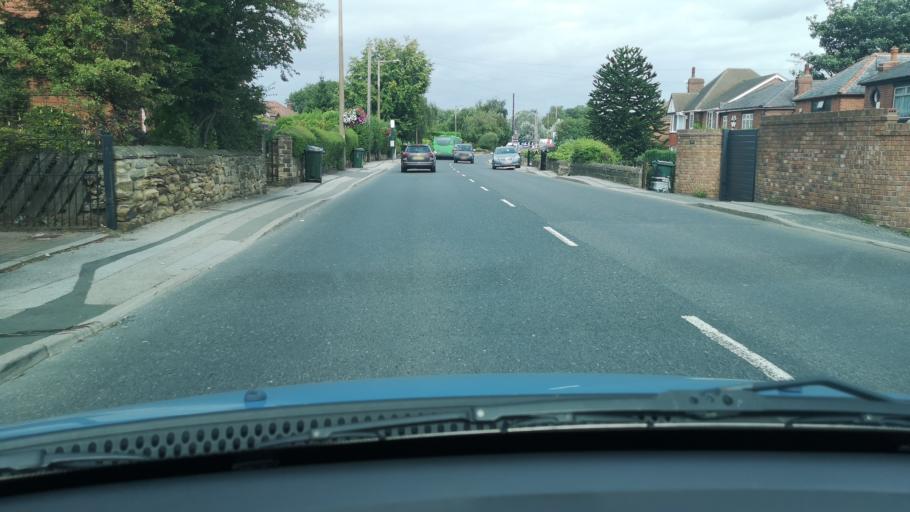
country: GB
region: England
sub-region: Barnsley
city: Shafton
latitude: 53.5867
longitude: -1.4089
